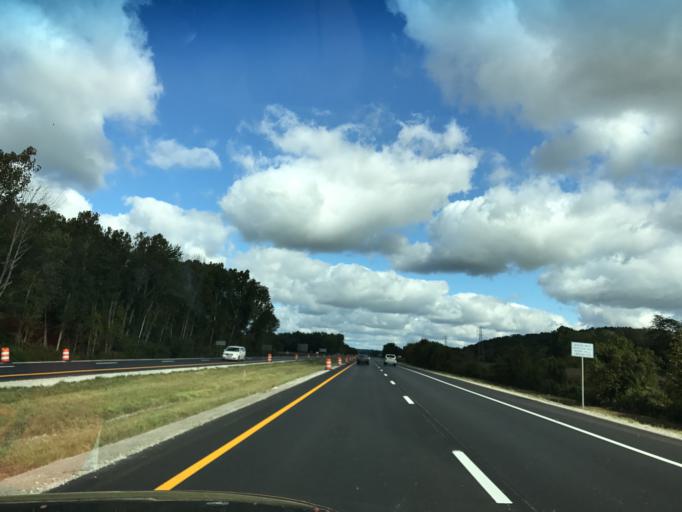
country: US
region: Ohio
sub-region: Fairfield County
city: Lancaster
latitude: 39.6269
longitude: -82.5518
